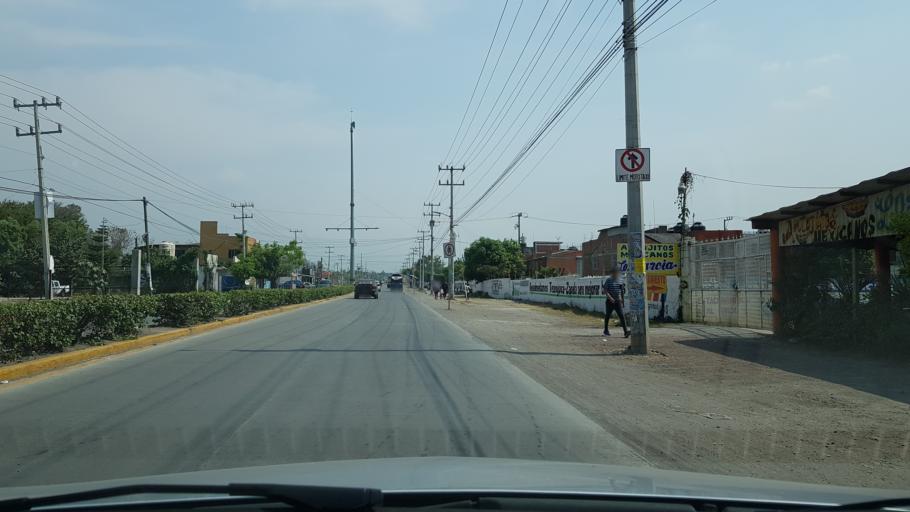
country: MX
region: Morelos
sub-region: Xochitepec
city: Chiconcuac
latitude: 18.8044
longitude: -99.1967
